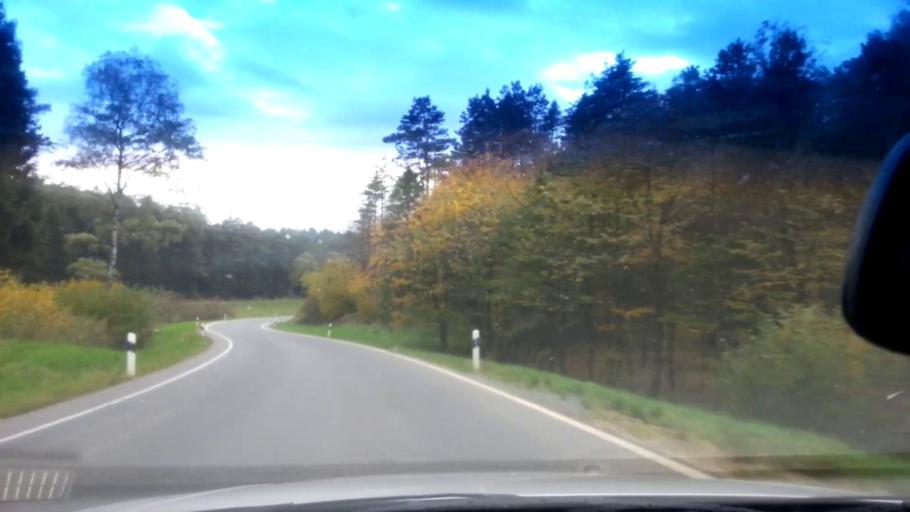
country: DE
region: Bavaria
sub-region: Upper Franconia
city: Wonsees
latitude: 50.0057
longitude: 11.3099
